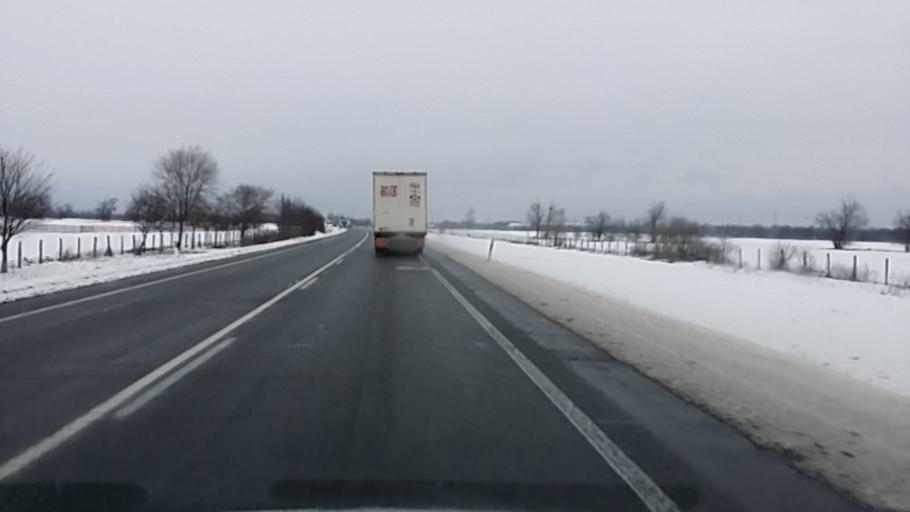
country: HU
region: Gyor-Moson-Sopron
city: Rajka
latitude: 47.9810
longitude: 17.1835
